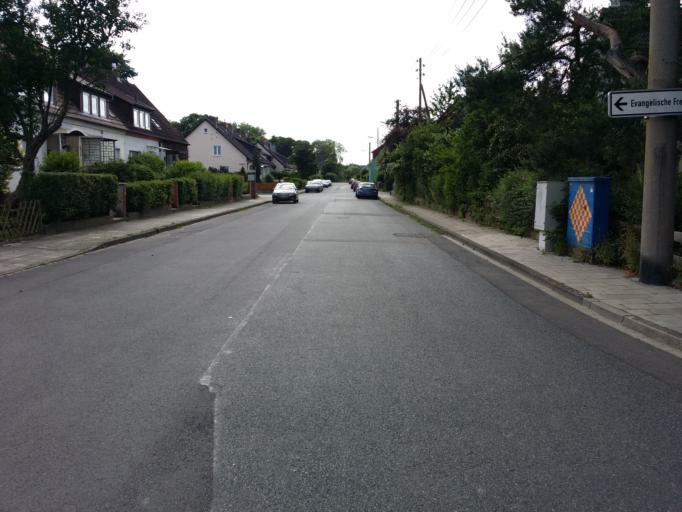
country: DE
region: Lower Saxony
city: Braunschweig
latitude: 52.2919
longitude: 10.5562
